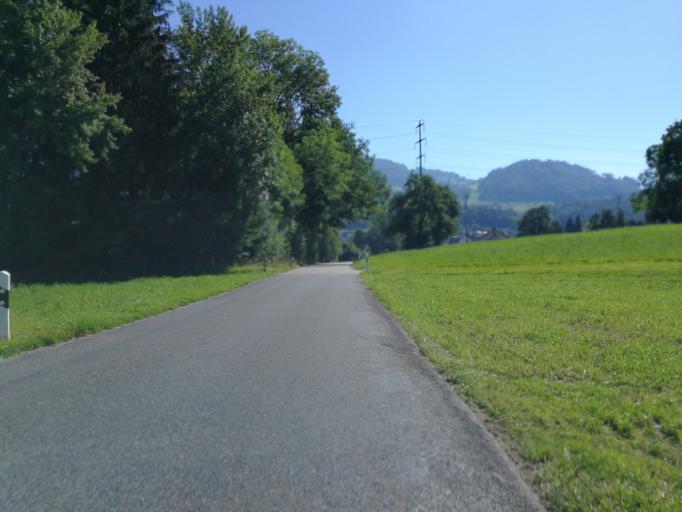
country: CH
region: Zurich
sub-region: Bezirk Hinwil
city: Hadlikon
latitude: 47.2874
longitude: 8.8505
